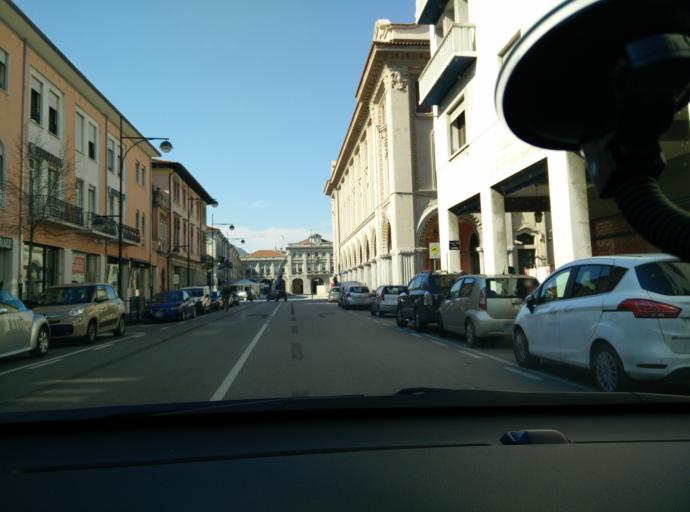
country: IT
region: Veneto
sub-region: Provincia di Venezia
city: San Dona di Piave
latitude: 45.6286
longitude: 12.5657
